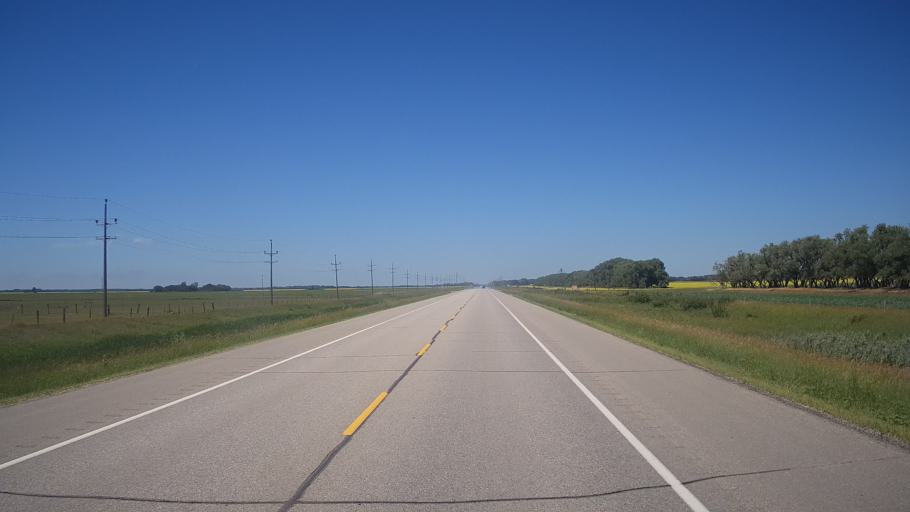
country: CA
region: Manitoba
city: Neepawa
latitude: 50.2257
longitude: -99.0613
